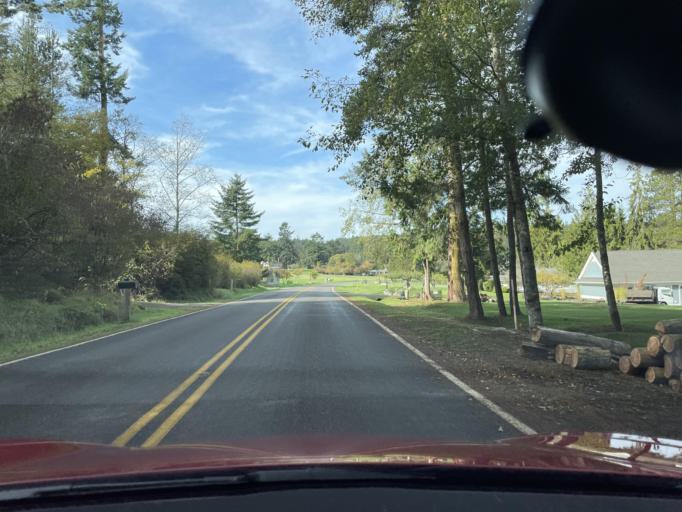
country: US
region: Washington
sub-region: San Juan County
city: Friday Harbor
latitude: 48.5263
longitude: -122.9781
